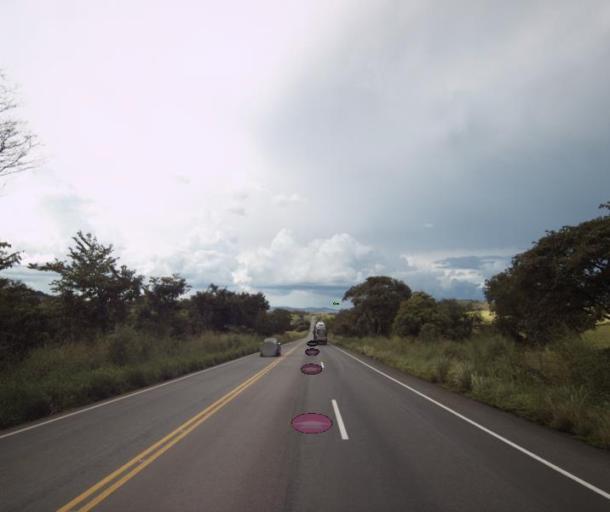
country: BR
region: Goias
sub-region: Rialma
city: Rialma
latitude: -15.2392
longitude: -49.5564
